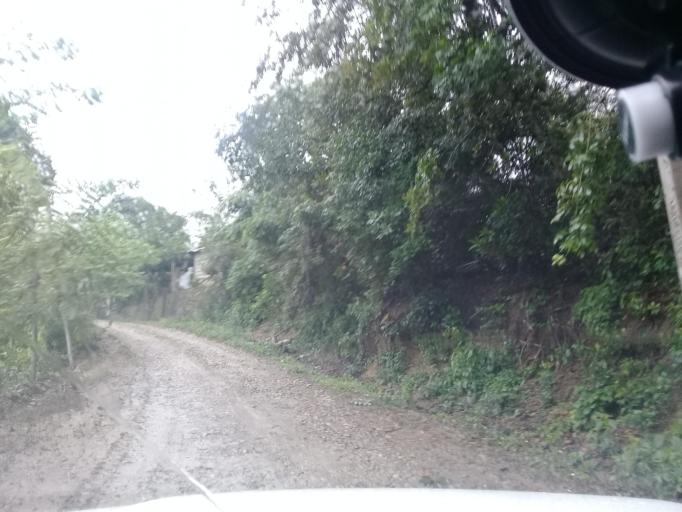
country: MX
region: Veracruz
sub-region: Chalma
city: San Pedro Coyutla
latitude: 21.2300
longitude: -98.4454
